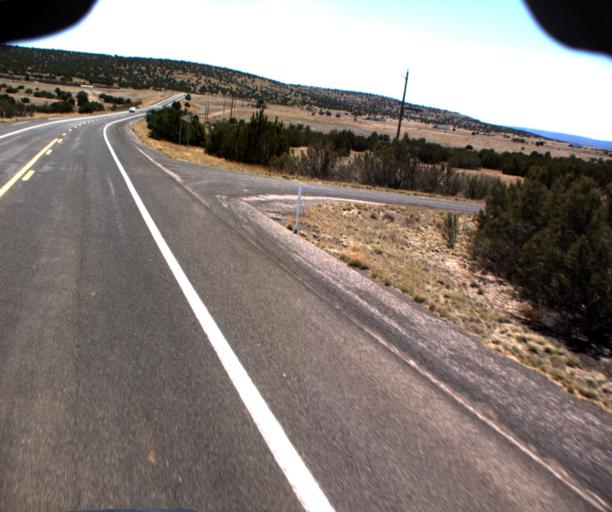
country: US
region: Arizona
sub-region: Mohave County
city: Peach Springs
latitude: 35.3261
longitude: -112.8910
